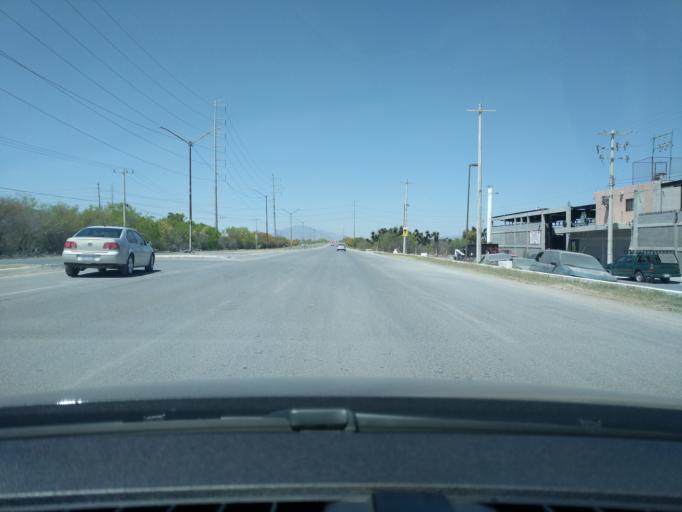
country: MX
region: Nuevo Leon
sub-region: Salinas Victoria
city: Emiliano Zapata
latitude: 25.9168
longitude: -100.2693
